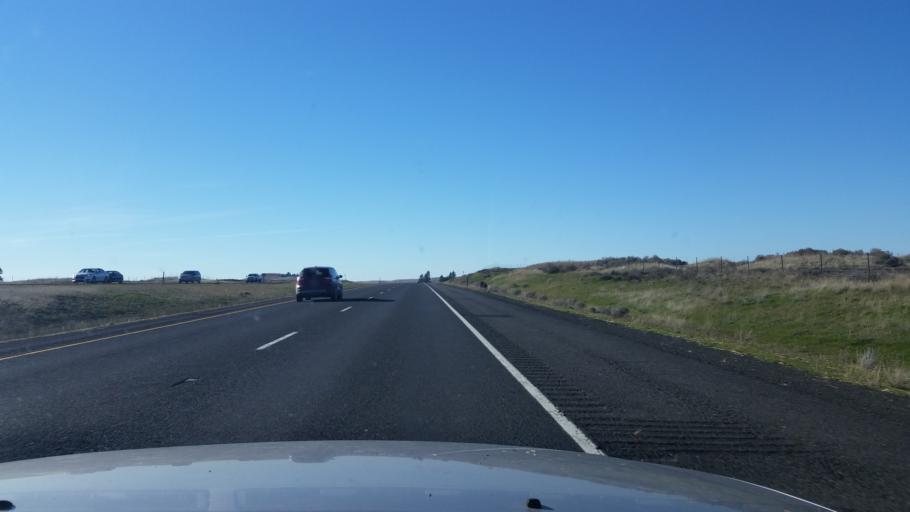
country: US
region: Washington
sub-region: Spokane County
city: Medical Lake
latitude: 47.3874
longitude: -117.8551
